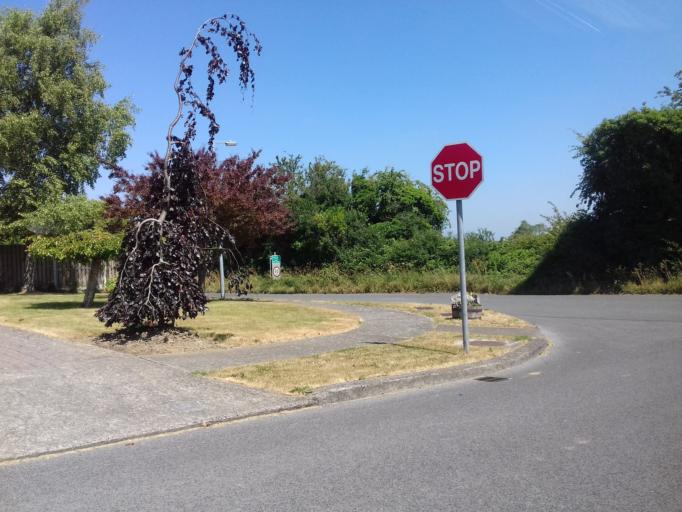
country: IE
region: Leinster
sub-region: An Mhi
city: Ashbourne
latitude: 53.5279
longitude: -6.3130
